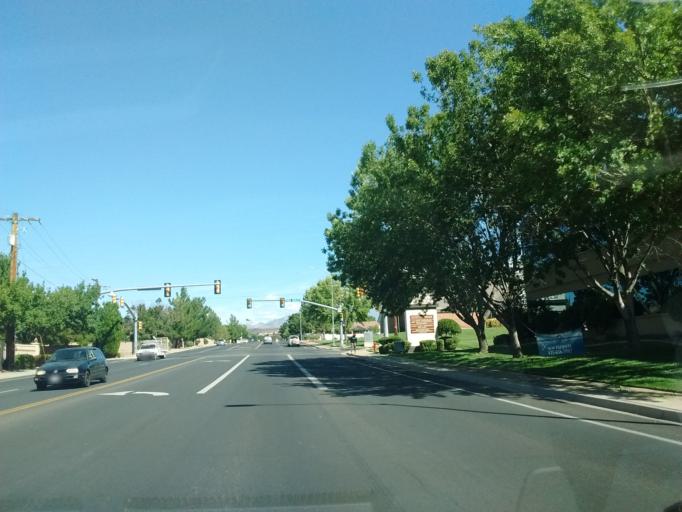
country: US
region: Utah
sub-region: Washington County
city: Saint George
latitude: 37.0918
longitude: -113.5570
